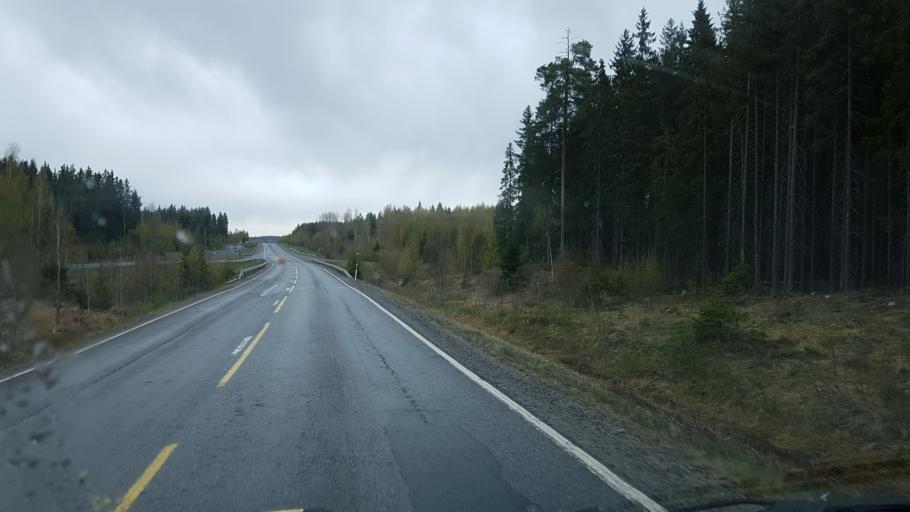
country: FI
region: Pirkanmaa
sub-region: Tampere
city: Pirkkala
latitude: 61.4079
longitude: 23.6337
